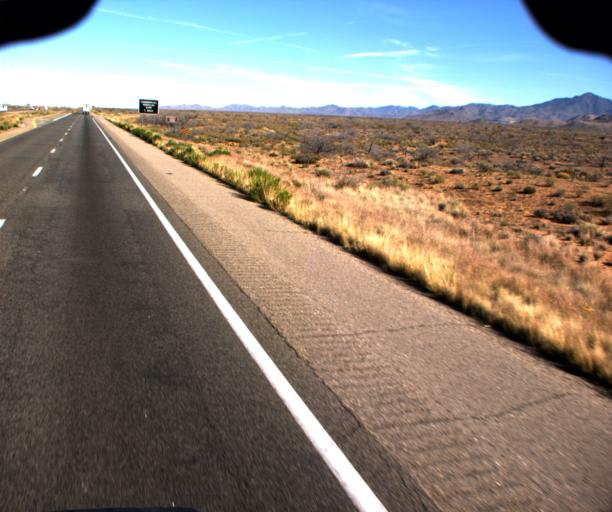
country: US
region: Arizona
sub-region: Mohave County
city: Golden Valley
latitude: 35.2790
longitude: -114.1738
